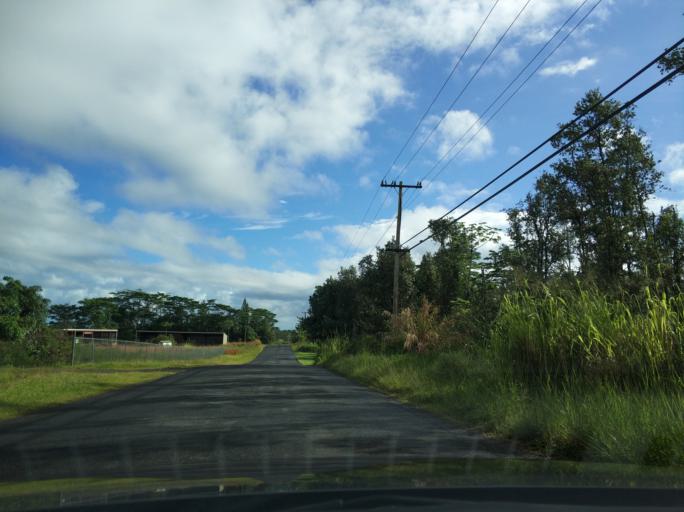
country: US
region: Hawaii
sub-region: Hawaii County
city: Orchidlands Estates
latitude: 19.5578
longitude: -154.9964
